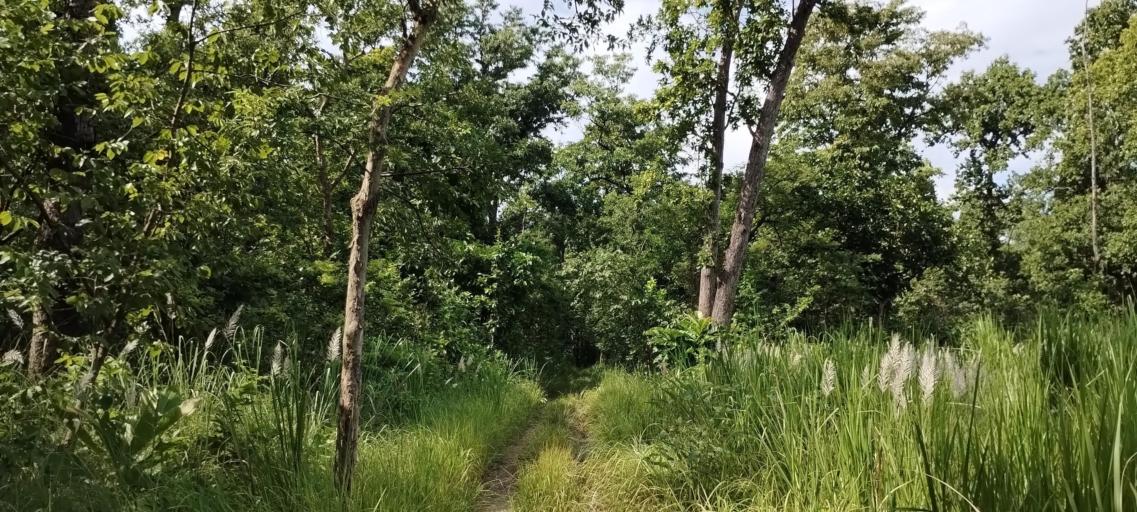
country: NP
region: Far Western
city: Tikapur
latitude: 28.5612
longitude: 81.2947
